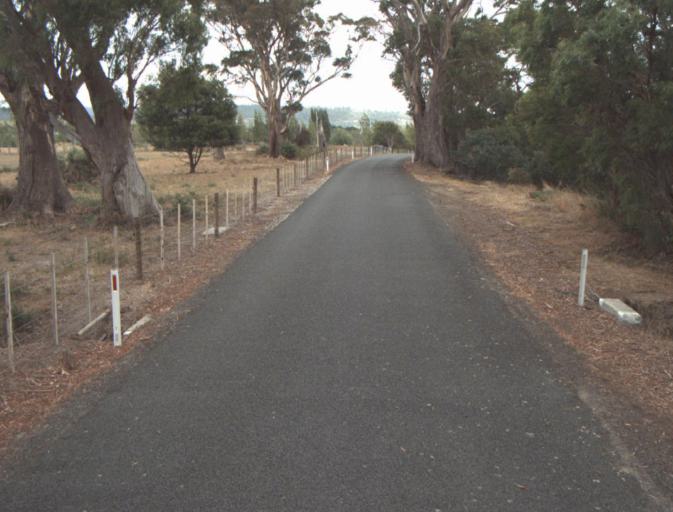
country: AU
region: Tasmania
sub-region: Launceston
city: Mayfield
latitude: -41.2874
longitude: 146.9963
